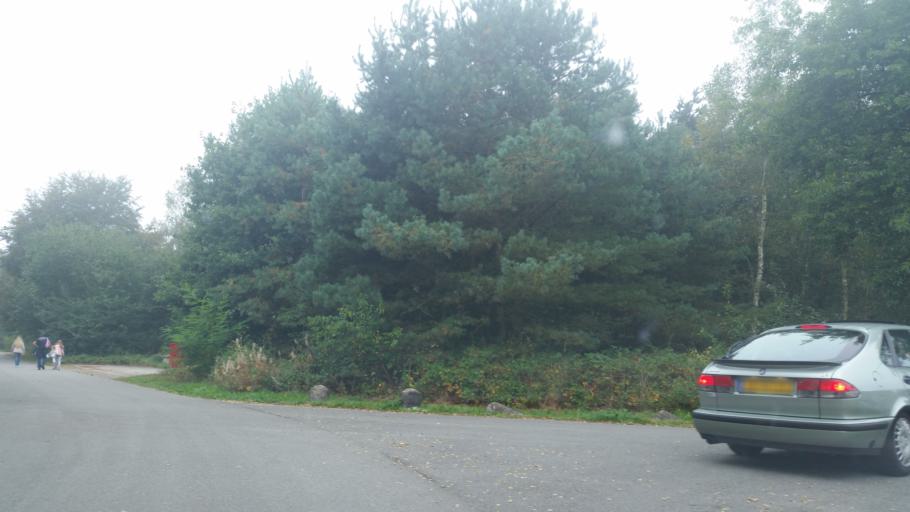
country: NL
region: Gelderland
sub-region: Gemeente Ede
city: Wekerom
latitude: 52.0677
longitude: 5.7035
